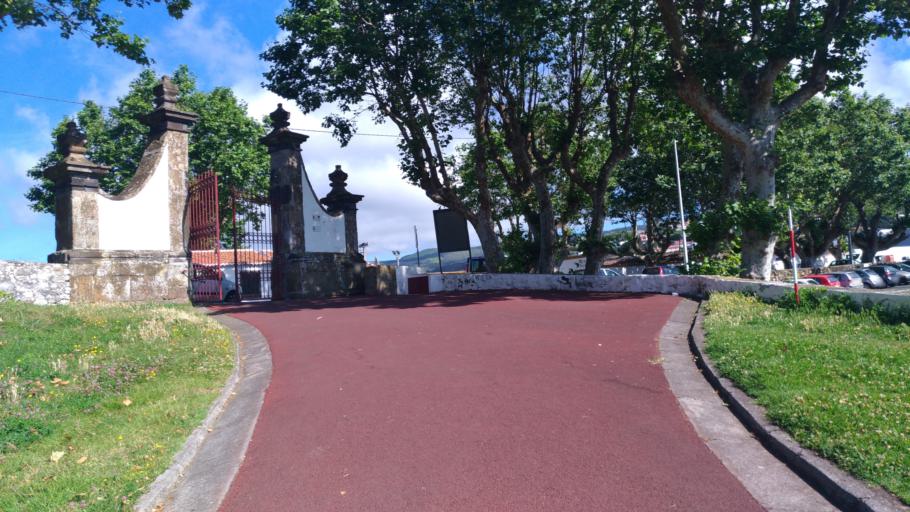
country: PT
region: Azores
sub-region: Angra do Heroismo
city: Angra do Heroismo
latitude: 38.6524
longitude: -27.2241
